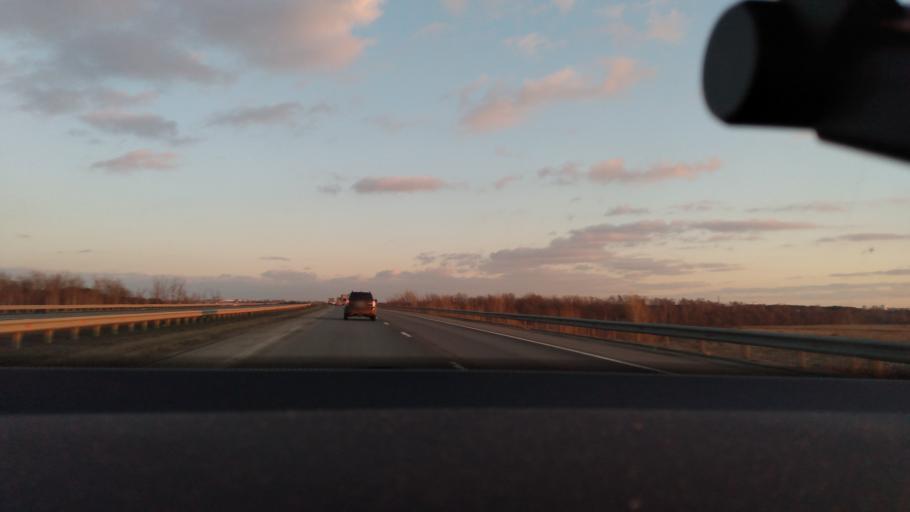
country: RU
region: Moskovskaya
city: Kolomna
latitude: 55.1303
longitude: 38.7807
